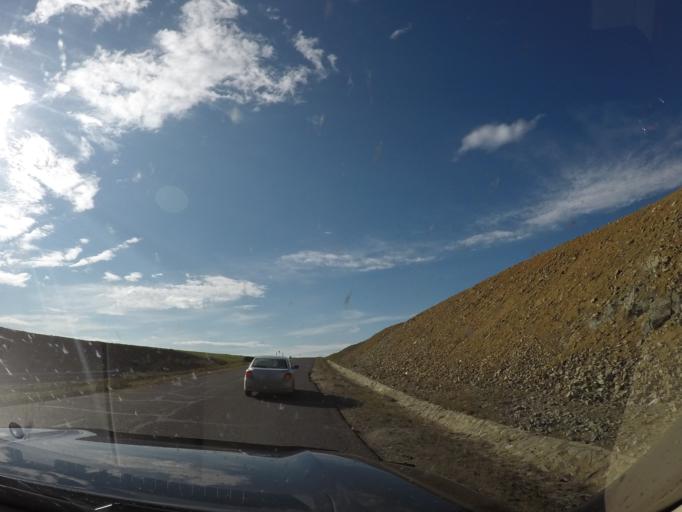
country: MN
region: Hentiy
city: Modot
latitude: 47.7939
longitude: 108.7643
